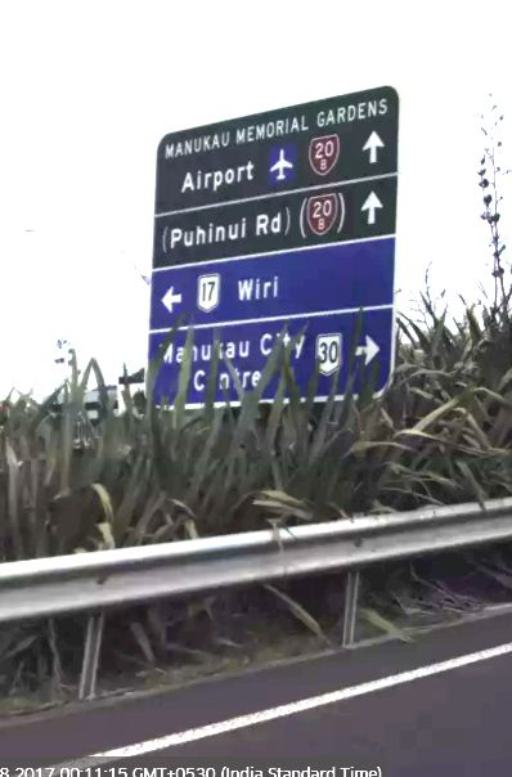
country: NZ
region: Auckland
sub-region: Auckland
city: Wiri
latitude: -36.9984
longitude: 174.8539
